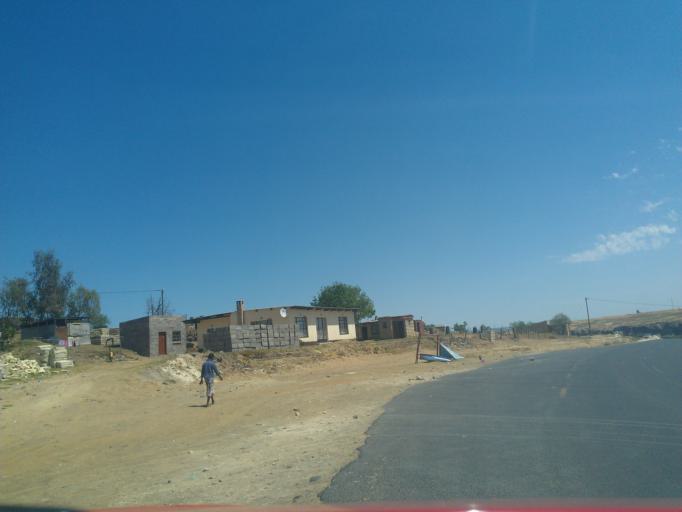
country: LS
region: Berea
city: Teyateyaneng
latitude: -29.1581
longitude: 27.6795
